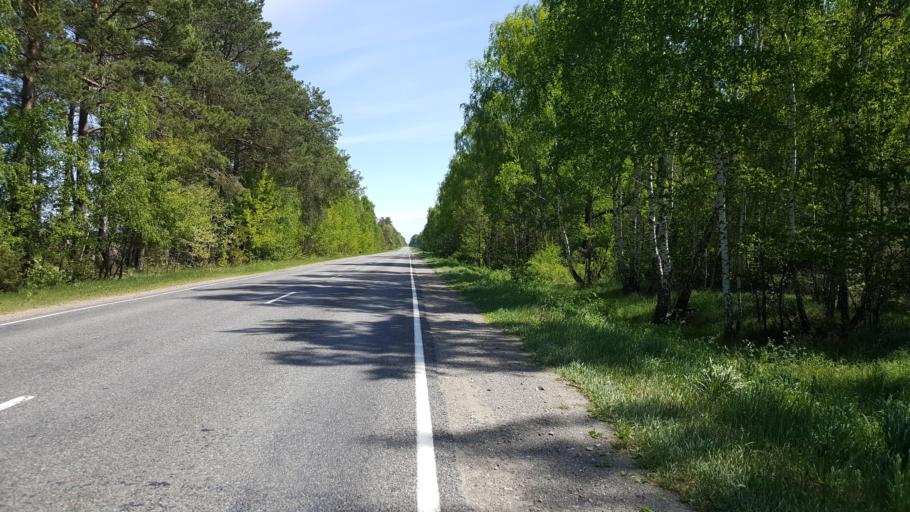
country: BY
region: Brest
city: Zhabinka
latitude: 52.3706
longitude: 24.0787
